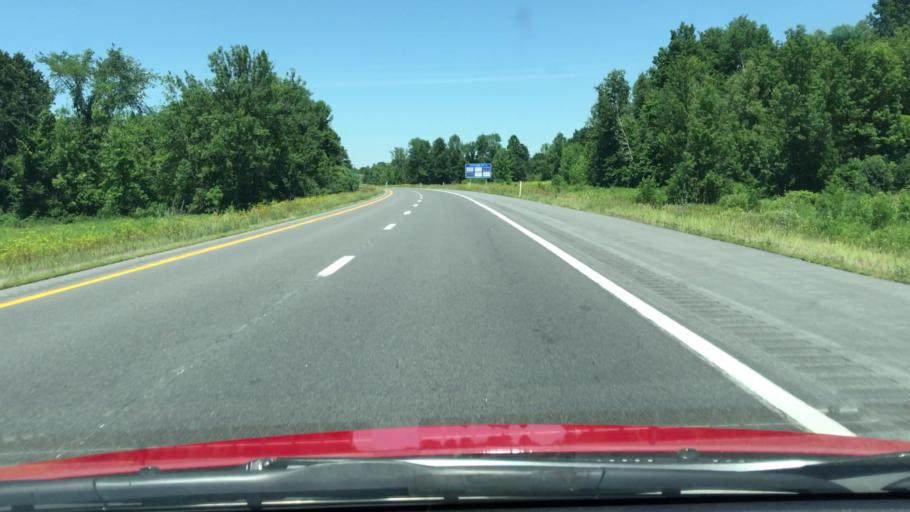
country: US
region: New York
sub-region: Clinton County
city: Champlain
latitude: 44.8635
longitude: -73.4494
